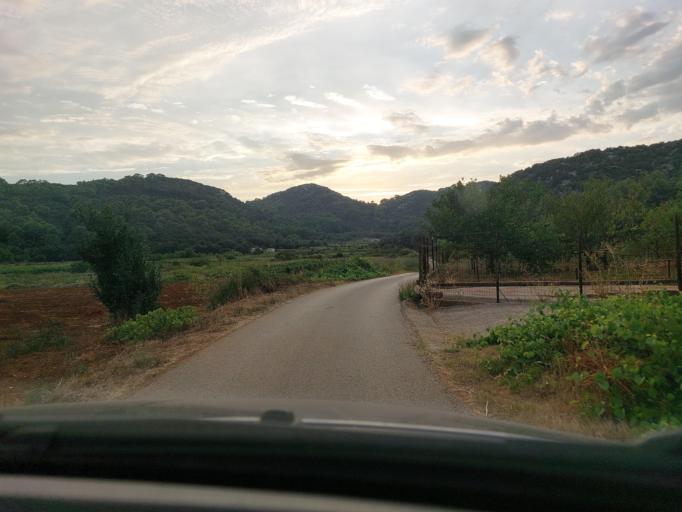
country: HR
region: Dubrovacko-Neretvanska
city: Smokvica
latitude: 42.7549
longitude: 16.9213
